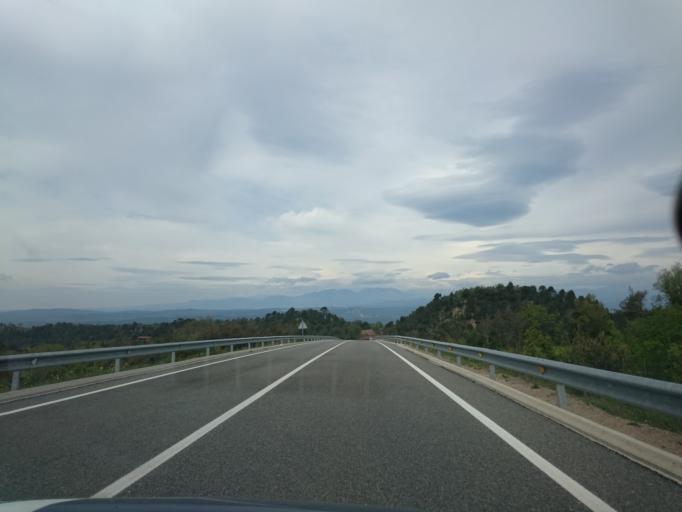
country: ES
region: Catalonia
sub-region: Provincia de Barcelona
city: Olost
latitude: 41.9588
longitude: 2.1334
